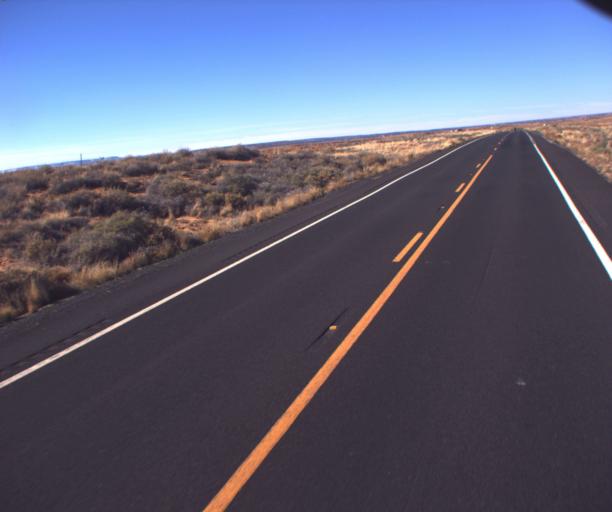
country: US
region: Arizona
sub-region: Coconino County
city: Kaibito
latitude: 36.4779
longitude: -110.7015
